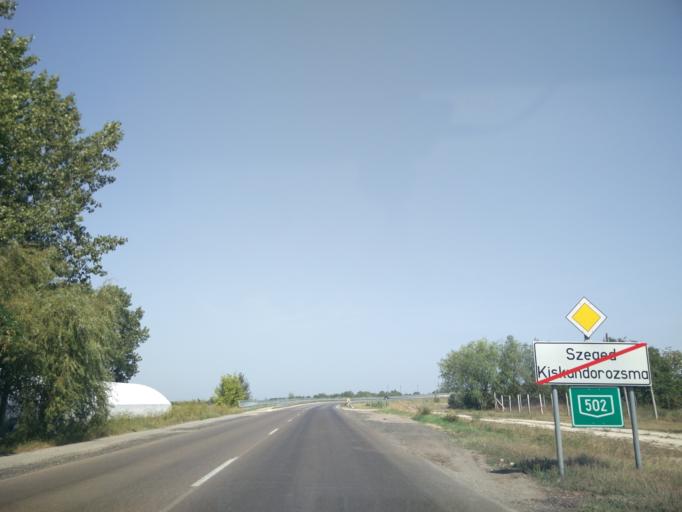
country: HU
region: Csongrad
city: Szeged
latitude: 46.2742
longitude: 20.0805
